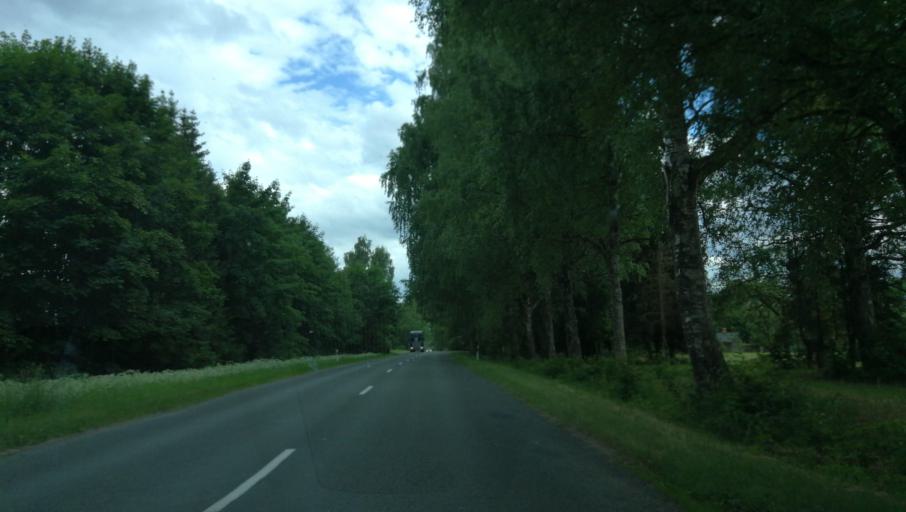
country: LV
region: Rujienas
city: Rujiena
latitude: 57.8585
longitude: 25.3746
